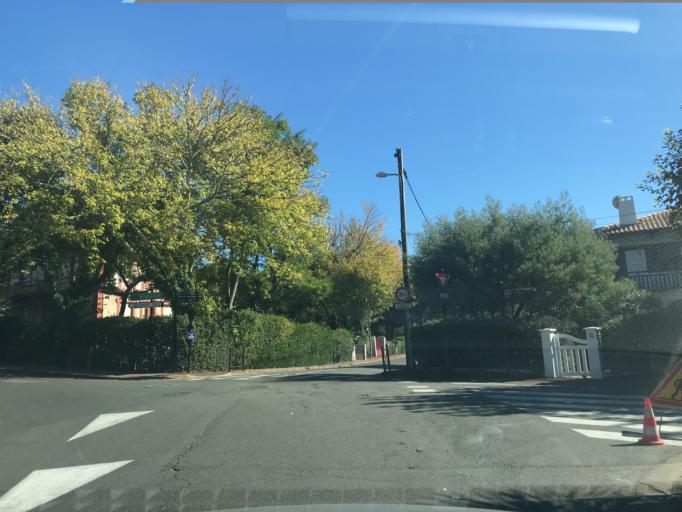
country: FR
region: Aquitaine
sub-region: Departement de la Gironde
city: Arcachon
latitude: 44.6551
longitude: -1.1759
